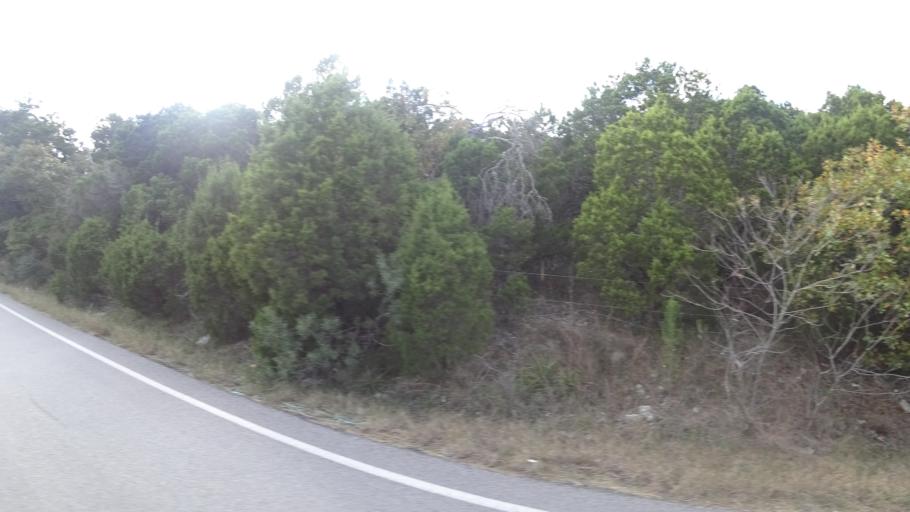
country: US
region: Texas
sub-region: Travis County
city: Barton Creek
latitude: 30.2699
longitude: -97.8872
